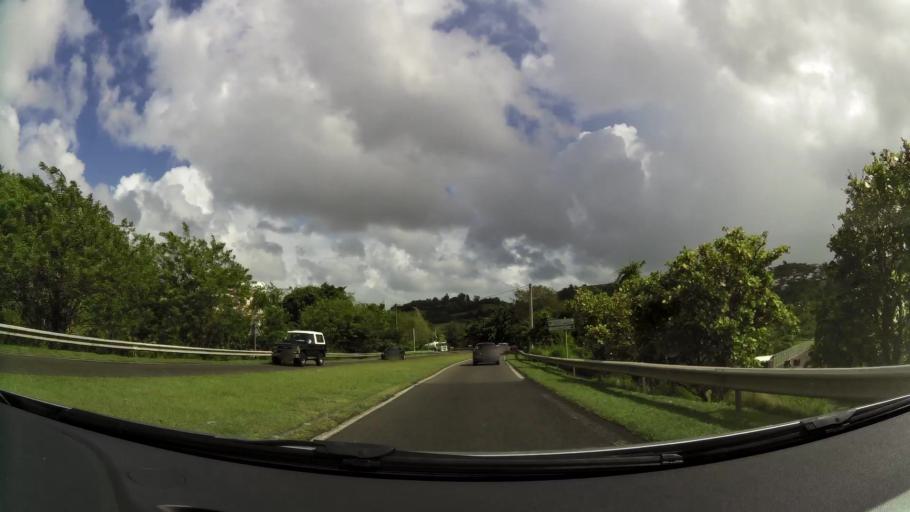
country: MQ
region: Martinique
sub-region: Martinique
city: Sainte-Luce
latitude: 14.5012
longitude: -60.9813
